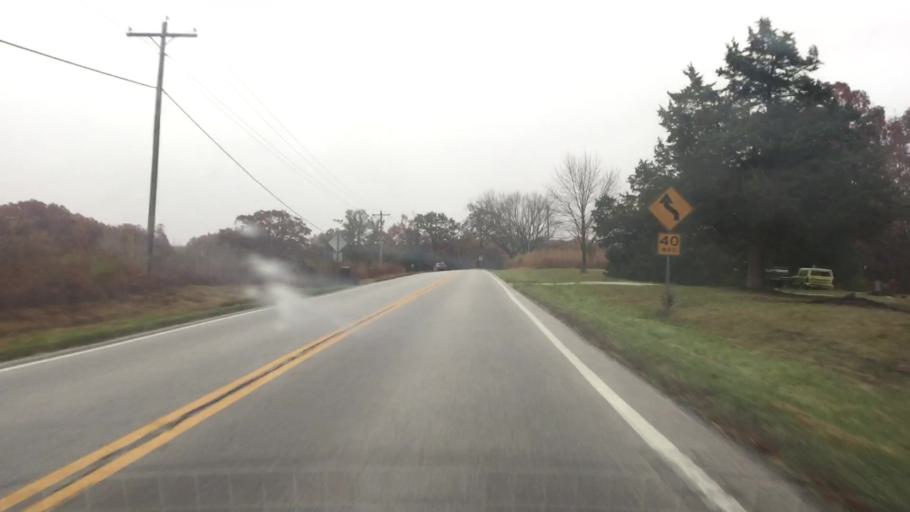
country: US
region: Missouri
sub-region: Callaway County
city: Fulton
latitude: 38.8792
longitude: -92.0851
